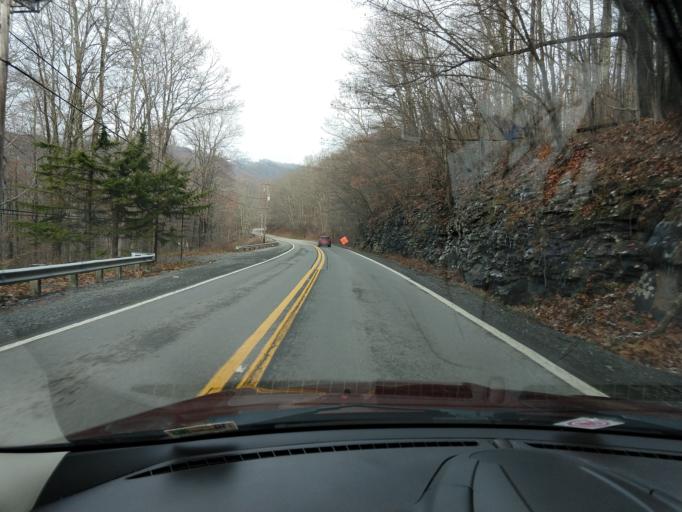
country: US
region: West Virginia
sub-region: Greenbrier County
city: Rainelle
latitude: 38.0317
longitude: -80.7279
